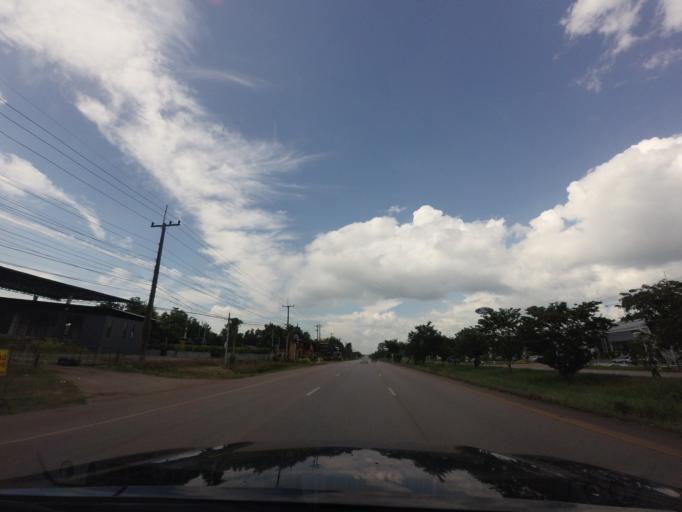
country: TH
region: Changwat Udon Thani
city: Udon Thani
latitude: 17.5393
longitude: 102.8001
